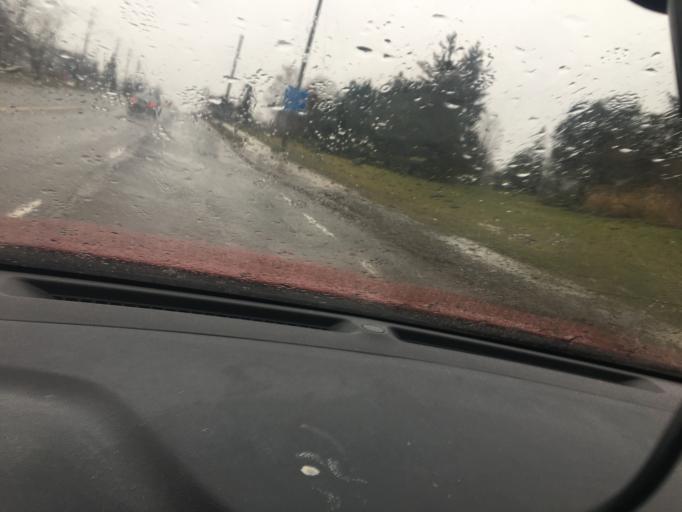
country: CA
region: Ontario
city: Scarborough
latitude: 43.7561
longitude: -79.2559
